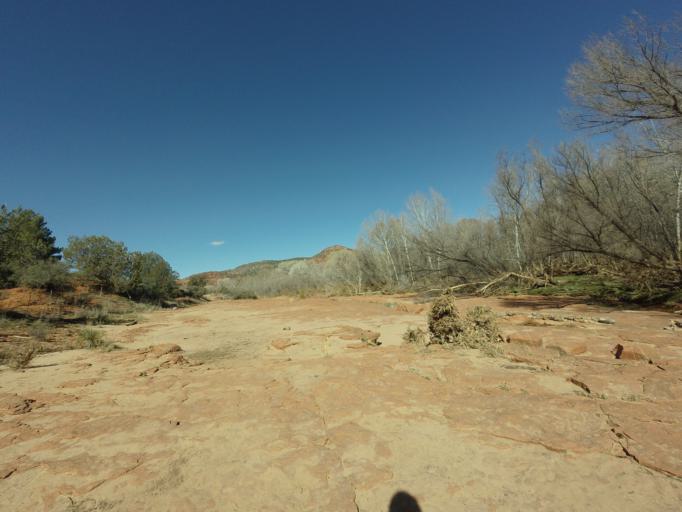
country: US
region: Arizona
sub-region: Yavapai County
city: West Sedona
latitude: 34.8245
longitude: -111.8065
